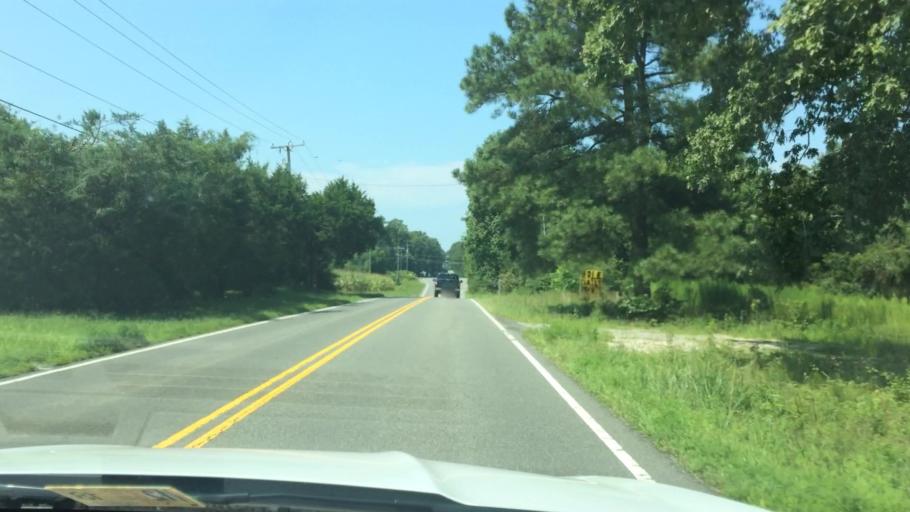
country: US
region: Virginia
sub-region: Henrico County
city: Sandston
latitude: 37.5275
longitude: -77.1651
